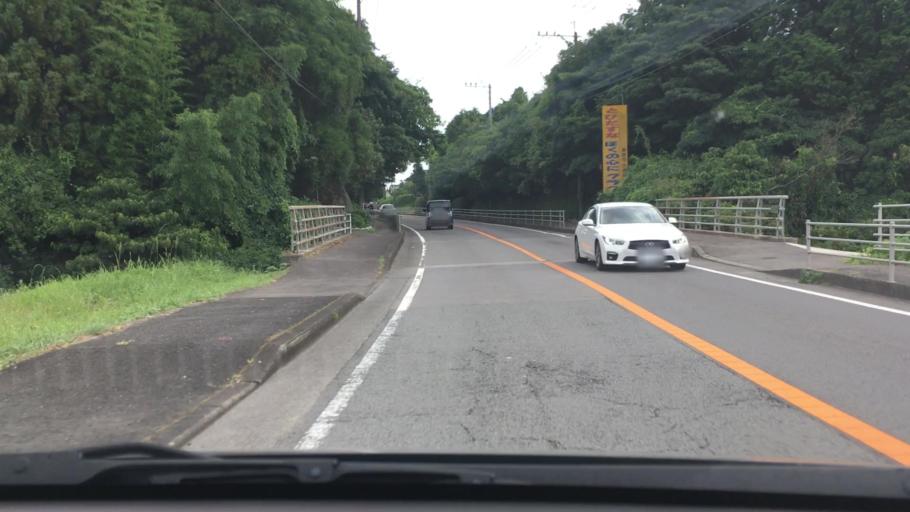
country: JP
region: Nagasaki
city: Togitsu
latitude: 32.9026
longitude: 129.7802
